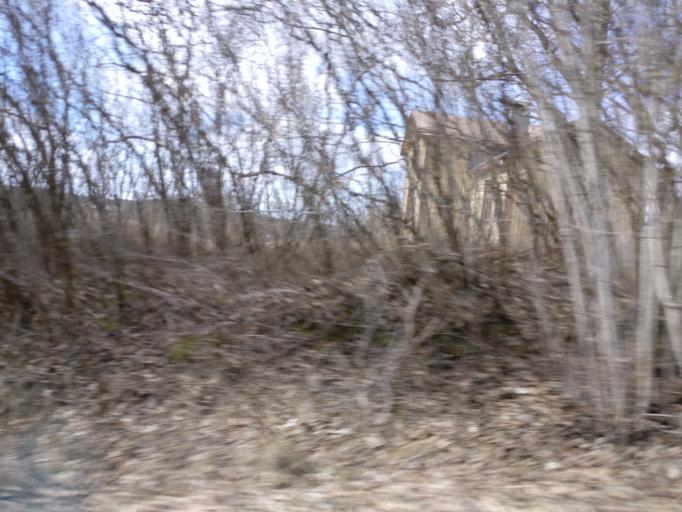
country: FI
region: Uusimaa
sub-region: Helsinki
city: Karjalohja
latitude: 60.2210
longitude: 23.7350
